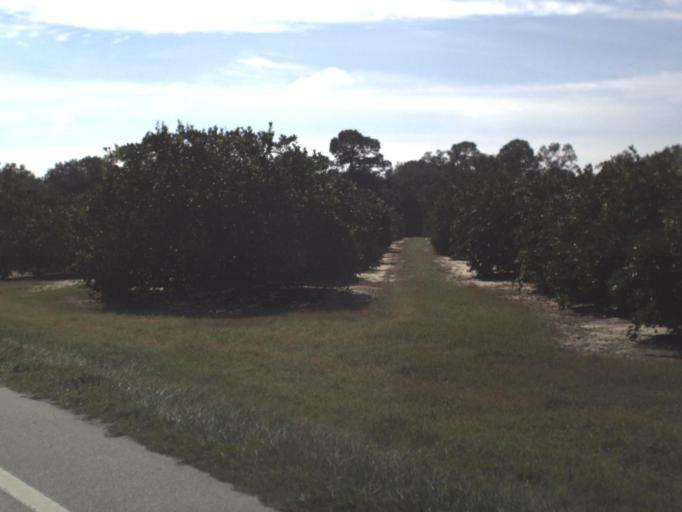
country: US
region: Florida
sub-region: Highlands County
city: Avon Park
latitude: 27.5852
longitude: -81.4712
